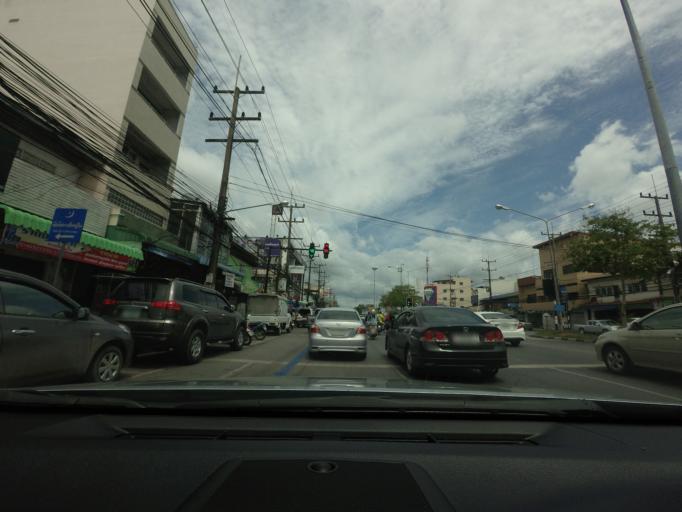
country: TH
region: Songkhla
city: Hat Yai
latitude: 7.0010
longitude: 100.4539
